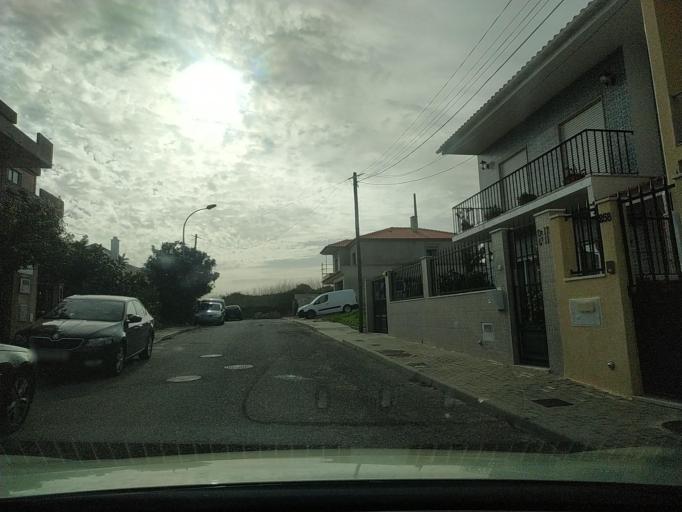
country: PT
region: Lisbon
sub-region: Sintra
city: Belas
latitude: 38.7775
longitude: -9.2434
